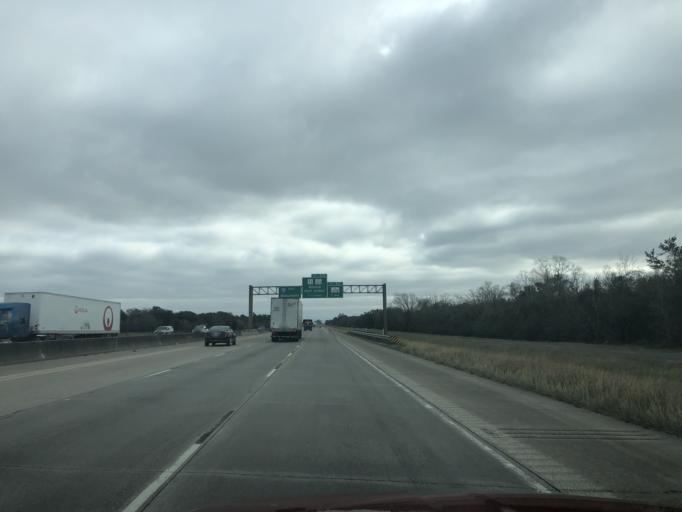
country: US
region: Texas
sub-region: Chambers County
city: Winnie
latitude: 29.8267
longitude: -94.4250
